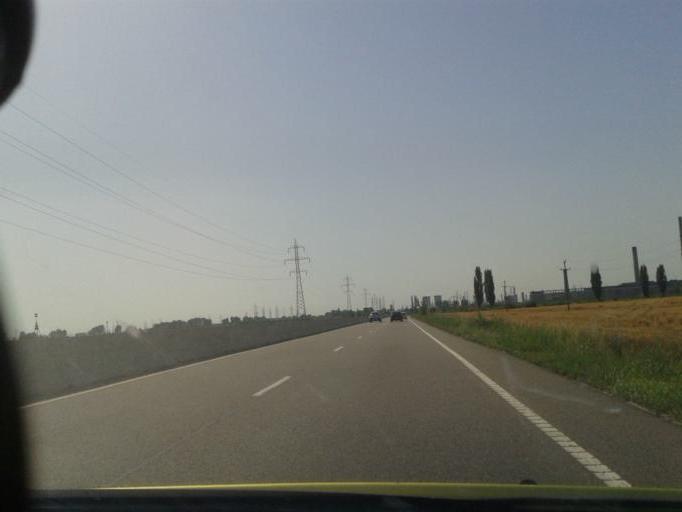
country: RO
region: Prahova
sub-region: Comuna Barcanesti
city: Tatarani
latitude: 44.8975
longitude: 26.0037
